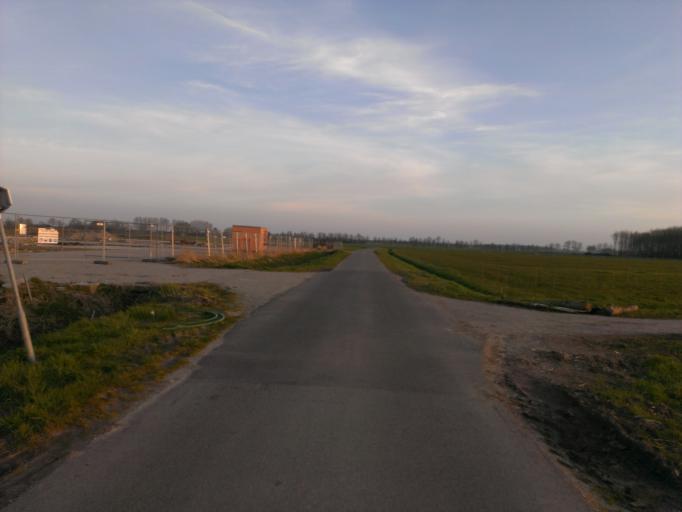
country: NL
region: Overijssel
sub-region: Gemeente Olst-Wijhe
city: Wijhe
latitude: 52.4020
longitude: 6.0941
